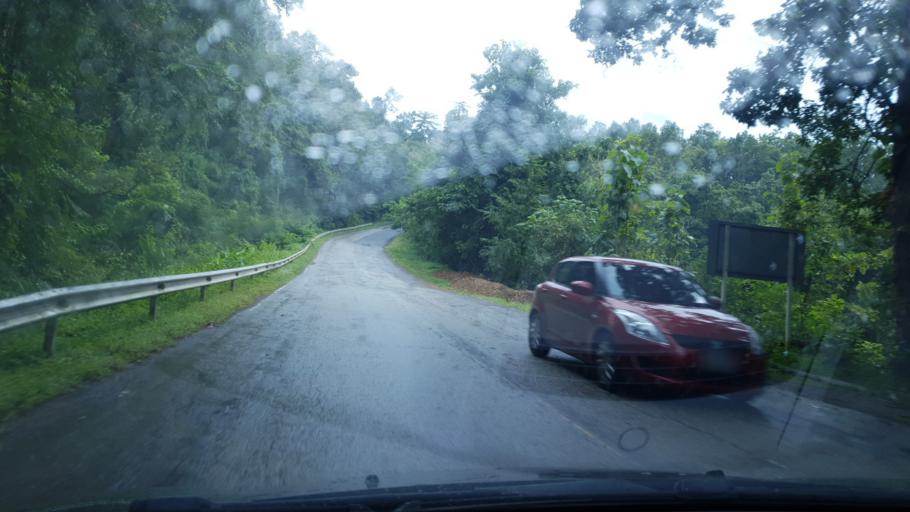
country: TH
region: Mae Hong Son
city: Pa Pae
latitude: 18.2753
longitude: 97.9387
